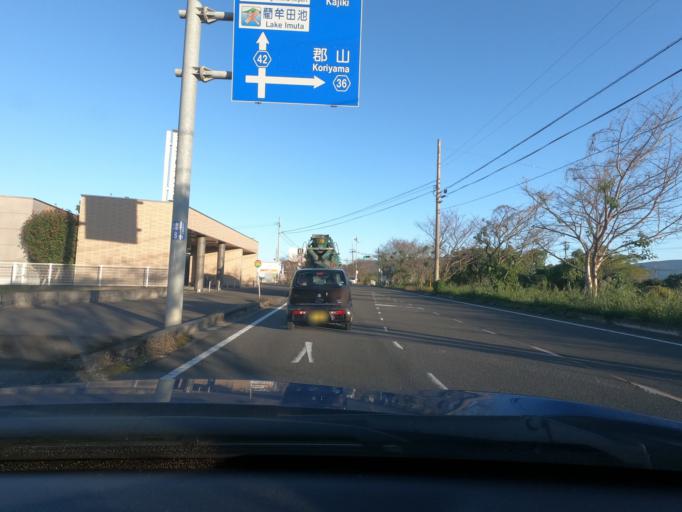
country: JP
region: Kagoshima
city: Satsumasendai
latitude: 31.8101
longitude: 130.3155
